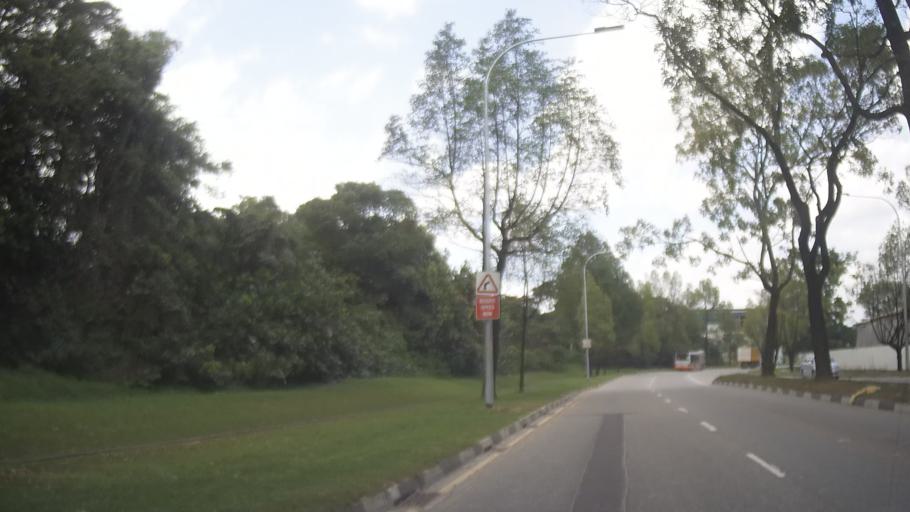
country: MY
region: Johor
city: Johor Bahru
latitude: 1.4291
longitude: 103.7471
